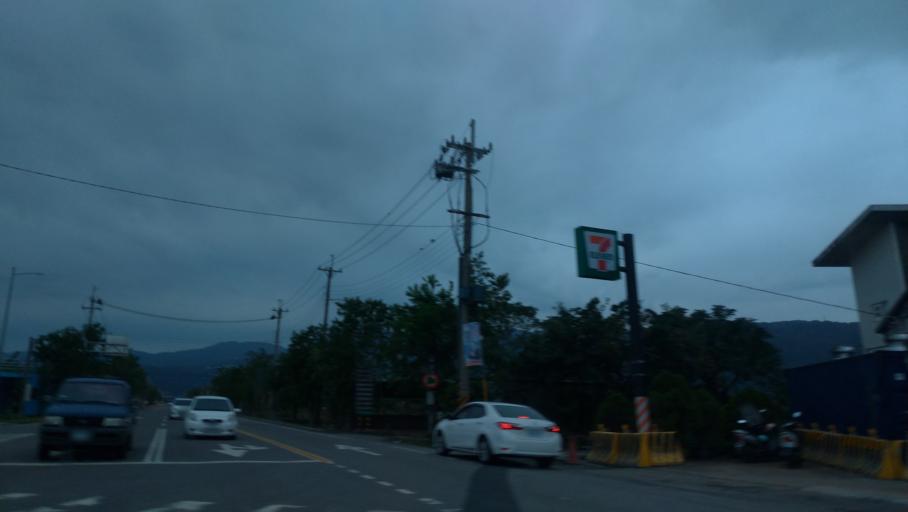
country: TW
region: Taiwan
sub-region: Yilan
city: Yilan
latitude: 24.8168
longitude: 121.7955
